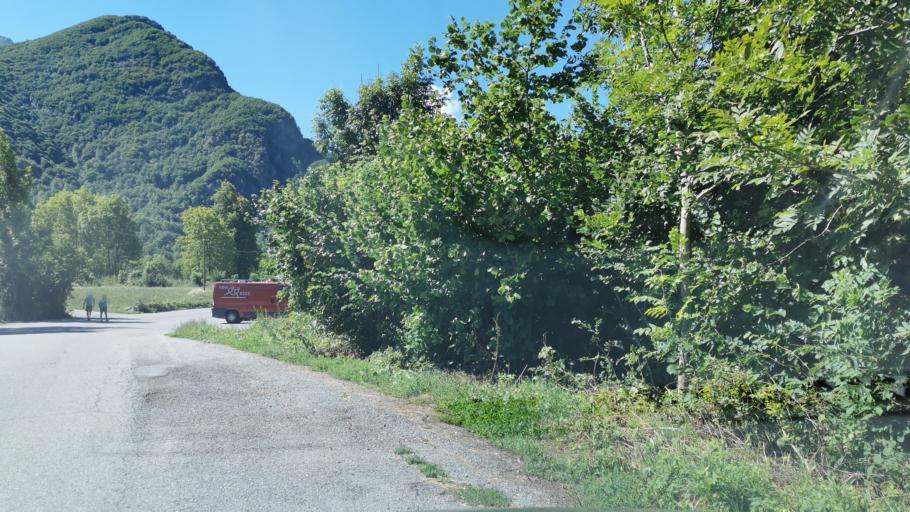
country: IT
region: Piedmont
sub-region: Provincia di Cuneo
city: Entracque
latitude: 44.2317
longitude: 7.3969
